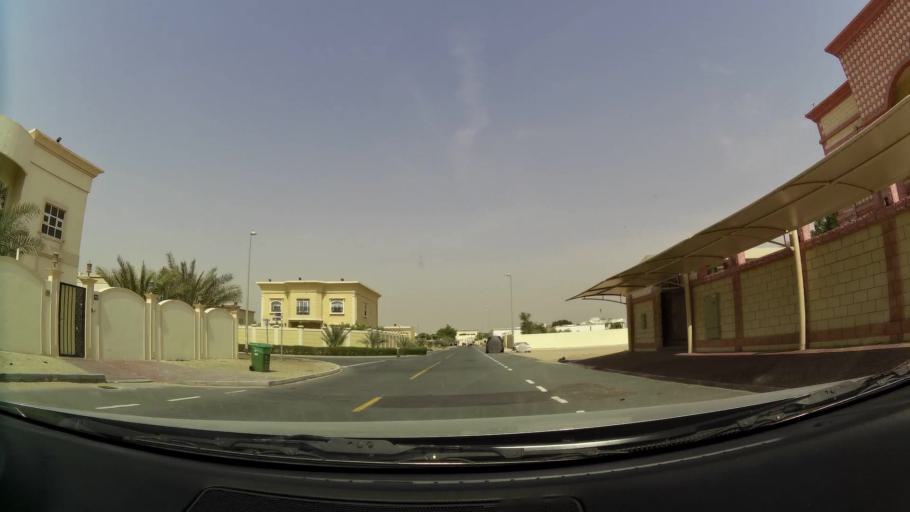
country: AE
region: Ash Shariqah
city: Sharjah
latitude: 25.2337
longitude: 55.4453
